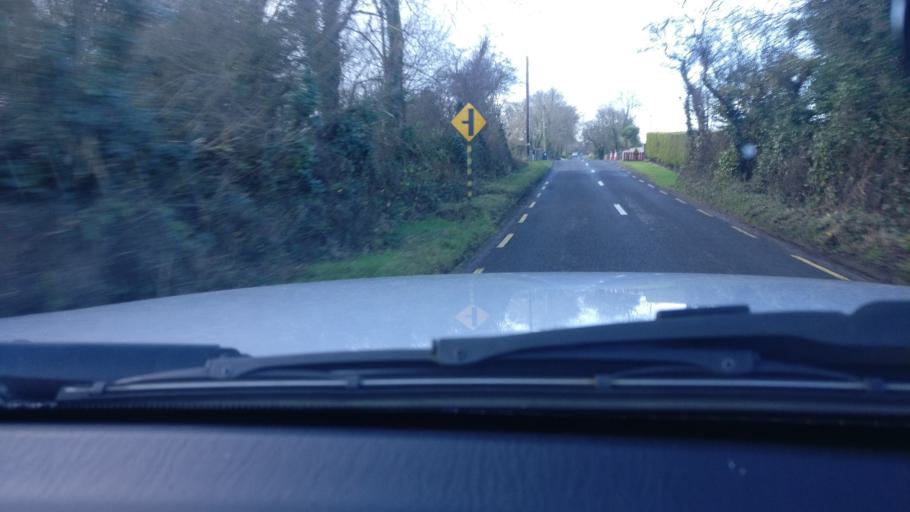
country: IE
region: Connaught
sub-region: County Galway
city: Ballinasloe
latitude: 53.2293
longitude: -8.3383
